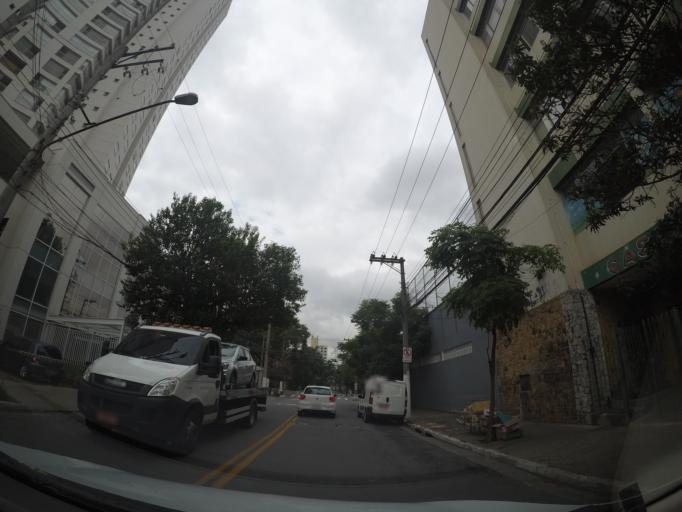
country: BR
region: Sao Paulo
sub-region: Sao Paulo
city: Sao Paulo
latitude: -23.5574
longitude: -46.6034
